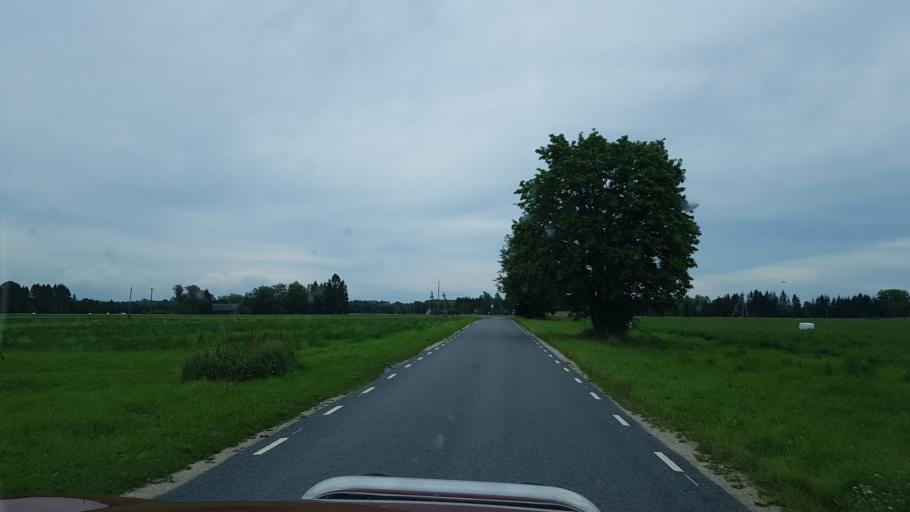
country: EE
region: Harju
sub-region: Nissi vald
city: Turba
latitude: 58.8772
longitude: 24.0810
